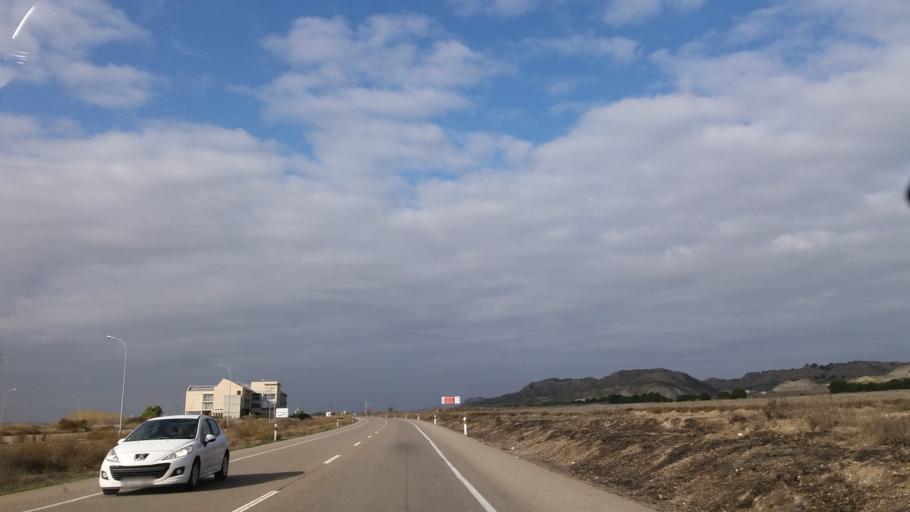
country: ES
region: Aragon
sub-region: Provincia de Zaragoza
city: Fuentes de Ebro
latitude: 41.5475
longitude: -0.5930
